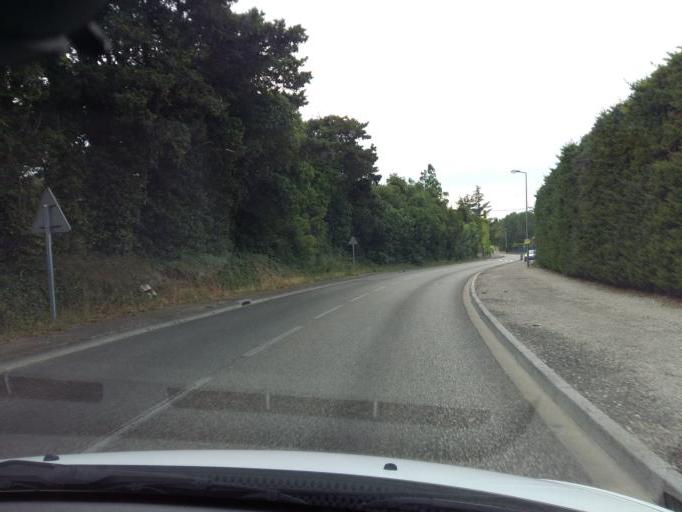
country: FR
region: Provence-Alpes-Cote d'Azur
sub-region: Departement du Vaucluse
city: Pernes-les-Fontaines
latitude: 43.9971
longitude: 5.0671
